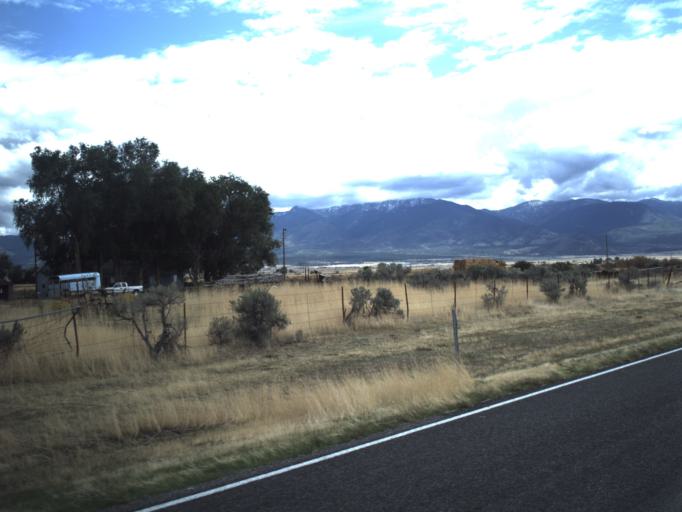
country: US
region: Utah
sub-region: Millard County
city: Fillmore
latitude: 38.9899
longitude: -112.4115
